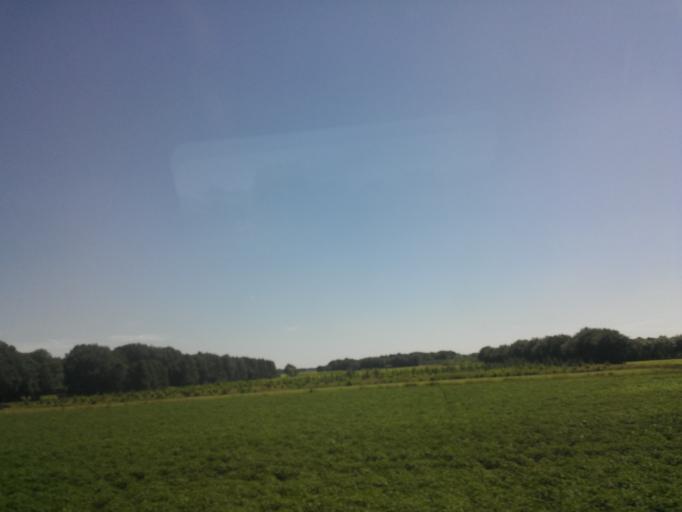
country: NL
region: Drenthe
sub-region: Gemeente Assen
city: Assen
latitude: 52.8935
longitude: 6.5352
